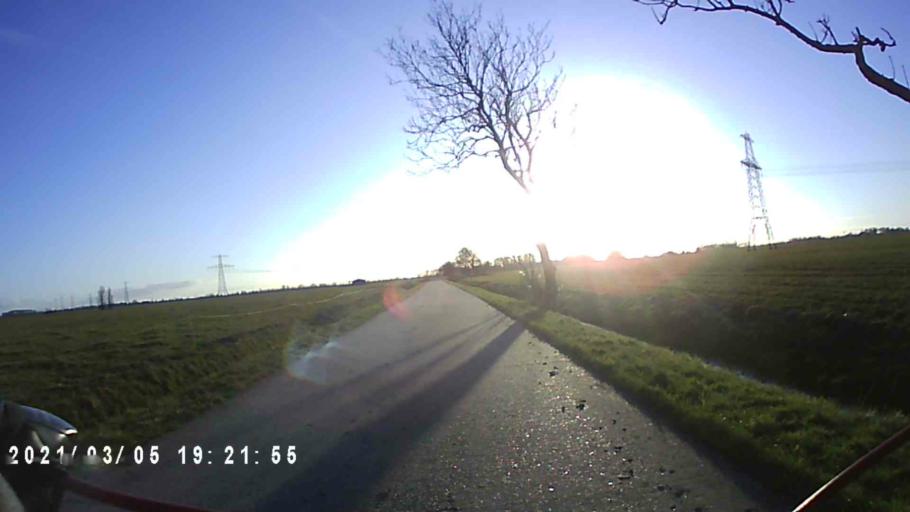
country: NL
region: Groningen
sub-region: Gemeente Winsum
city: Winsum
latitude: 53.3275
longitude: 6.4962
